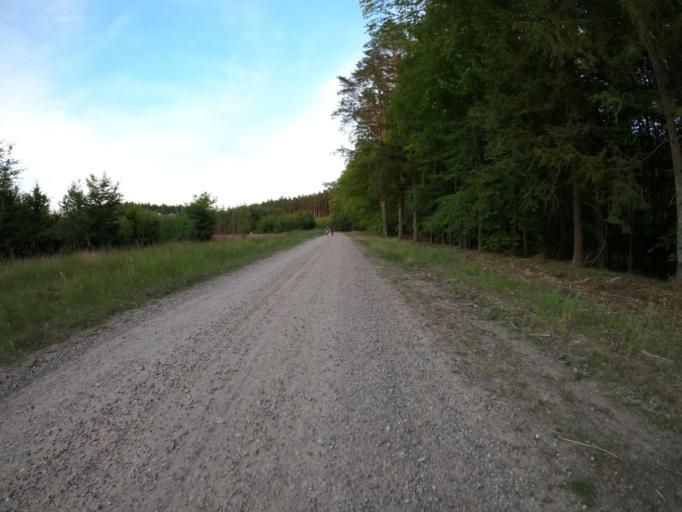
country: PL
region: West Pomeranian Voivodeship
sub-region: Powiat koszalinski
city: Sianow
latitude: 54.0999
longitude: 16.3972
